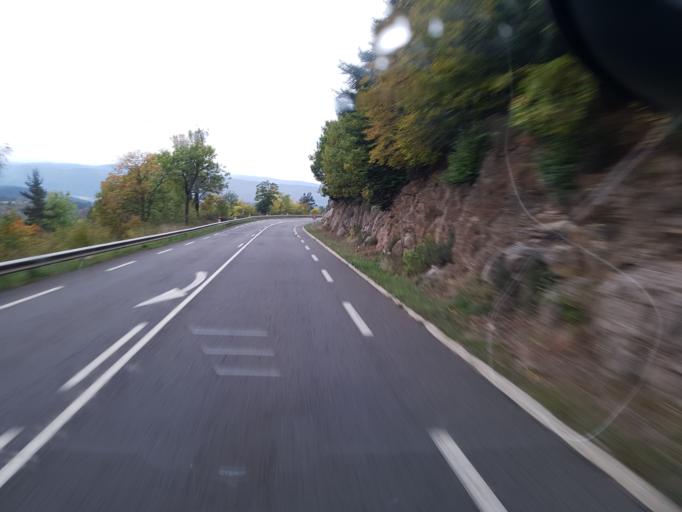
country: FR
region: Languedoc-Roussillon
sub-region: Departement de la Lozere
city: Mende
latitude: 44.5481
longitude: 3.6197
